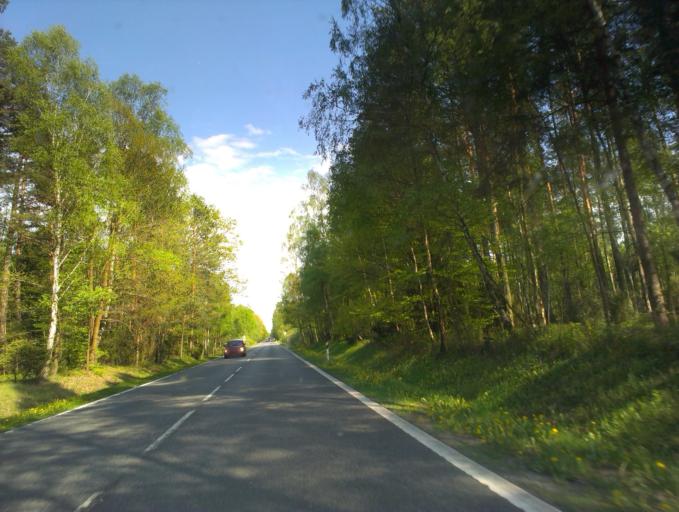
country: PL
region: Kujawsko-Pomorskie
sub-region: Powiat swiecki
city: Swiekatowo
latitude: 53.4899
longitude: 18.0975
